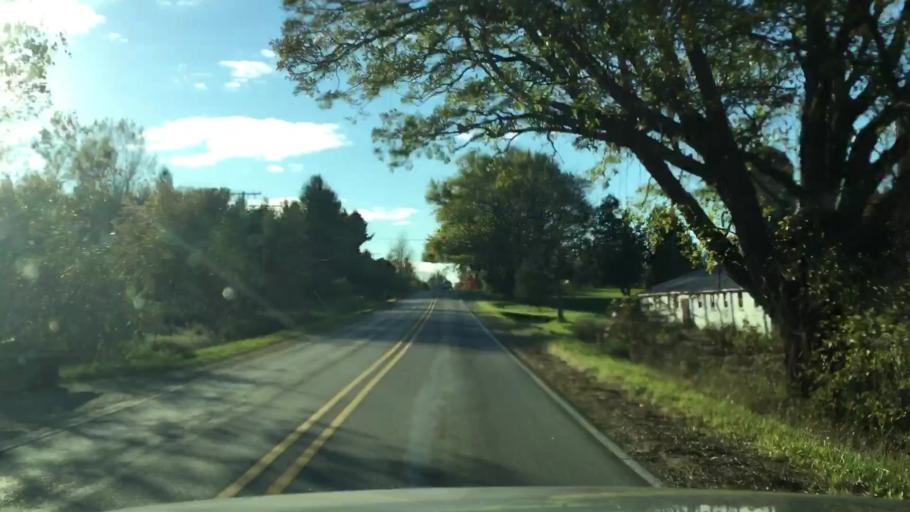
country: US
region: Michigan
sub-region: Lapeer County
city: Imlay City
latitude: 43.0033
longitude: -83.1697
